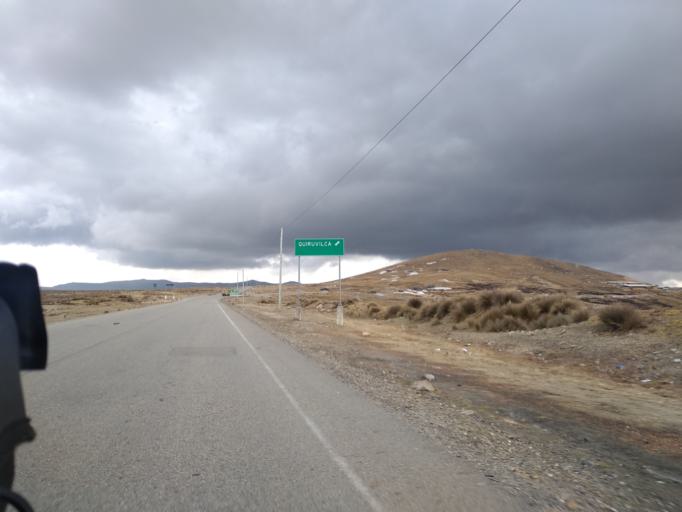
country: PE
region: La Libertad
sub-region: Provincia de Santiago de Chuco
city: Quiruvilca
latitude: -7.9915
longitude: -78.2920
